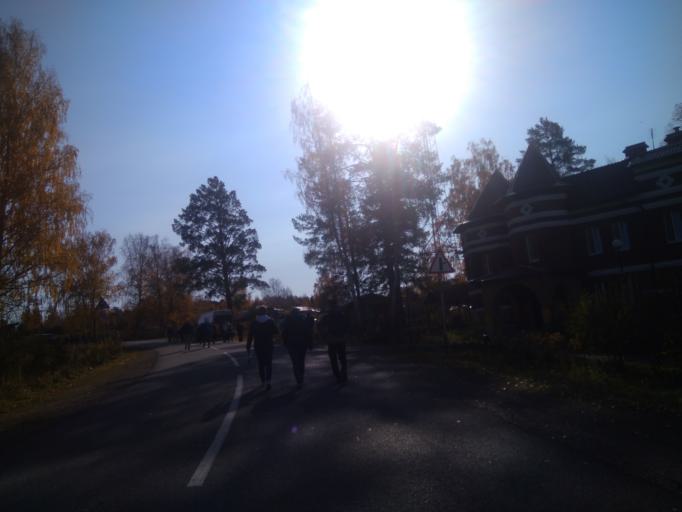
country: RU
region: Sverdlovsk
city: Mikhaylovsk
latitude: 56.5255
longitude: 59.2266
